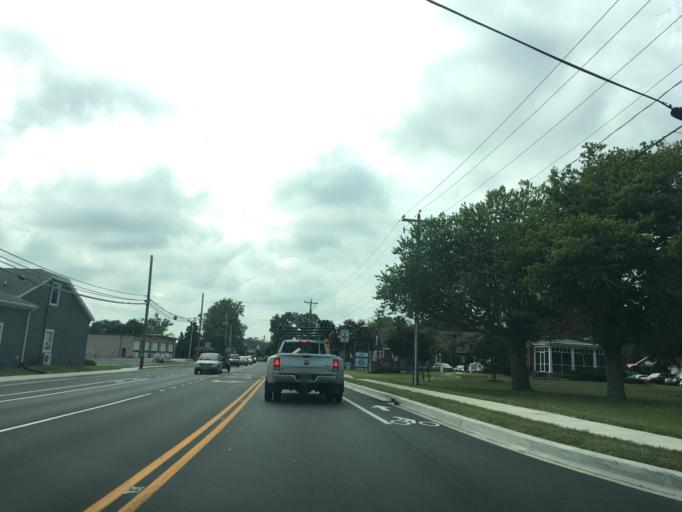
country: US
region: Delaware
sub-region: Sussex County
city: Ocean View
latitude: 38.5474
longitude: -75.1087
